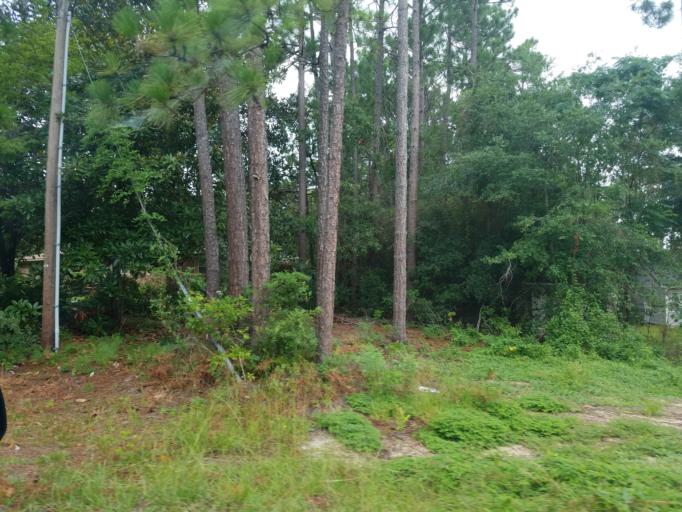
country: US
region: North Carolina
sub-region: New Hanover County
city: Kings Grant
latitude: 34.2371
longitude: -77.8614
